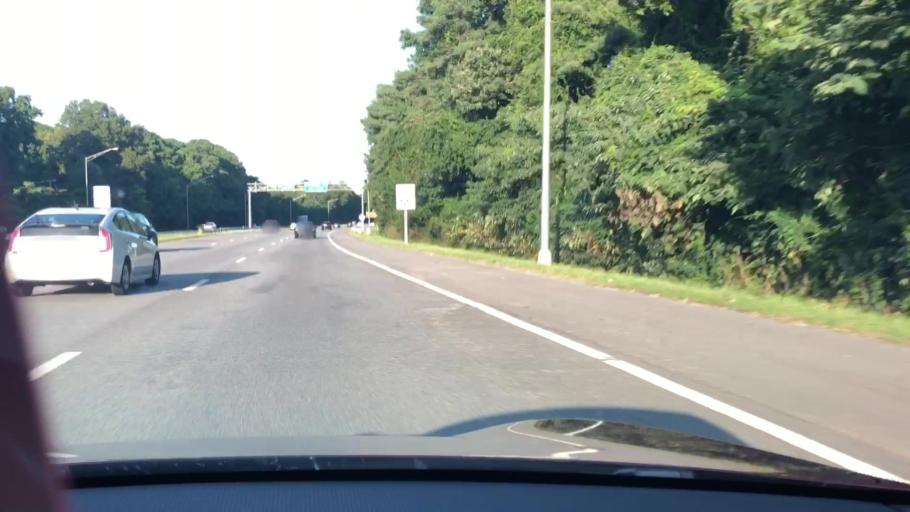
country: US
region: Virginia
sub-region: City of Virginia Beach
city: Virginia Beach
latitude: 36.8468
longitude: -76.0148
